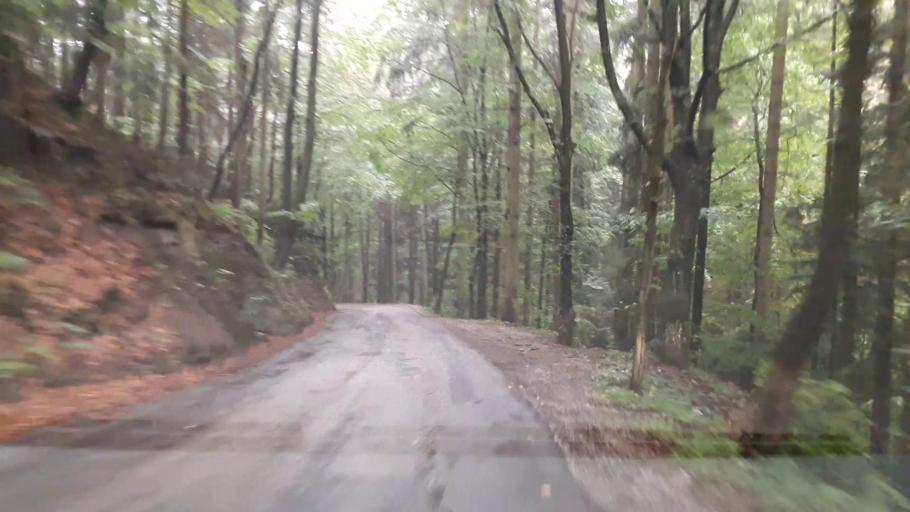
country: AT
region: Lower Austria
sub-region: Politischer Bezirk Krems
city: Aggsbach
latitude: 48.2926
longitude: 15.3686
